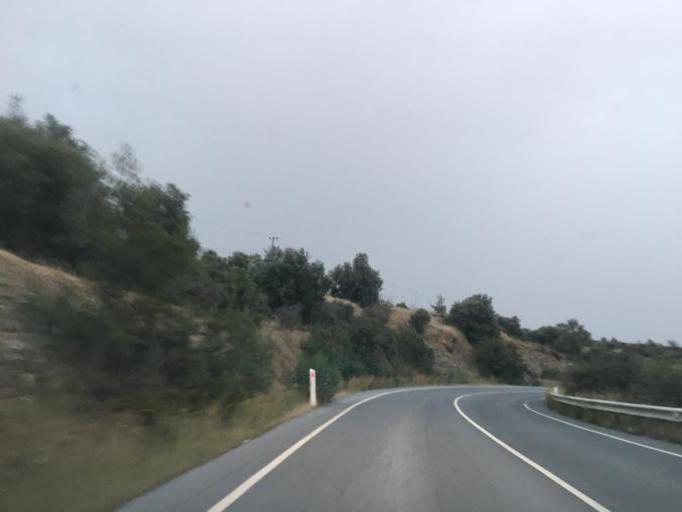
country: CY
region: Limassol
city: Parekklisha
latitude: 34.7758
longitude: 33.1619
